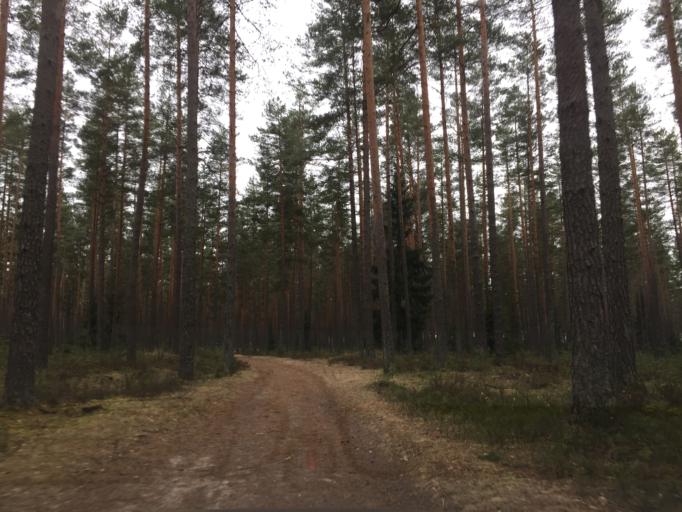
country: LV
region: Garkalne
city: Garkalne
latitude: 56.9696
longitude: 24.4311
